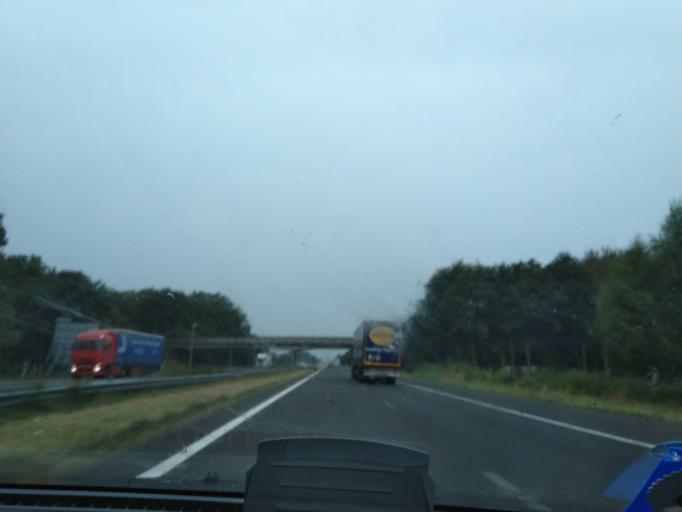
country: NL
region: Drenthe
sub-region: Gemeente Emmen
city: Klazienaveen
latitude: 52.7337
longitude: 7.0121
